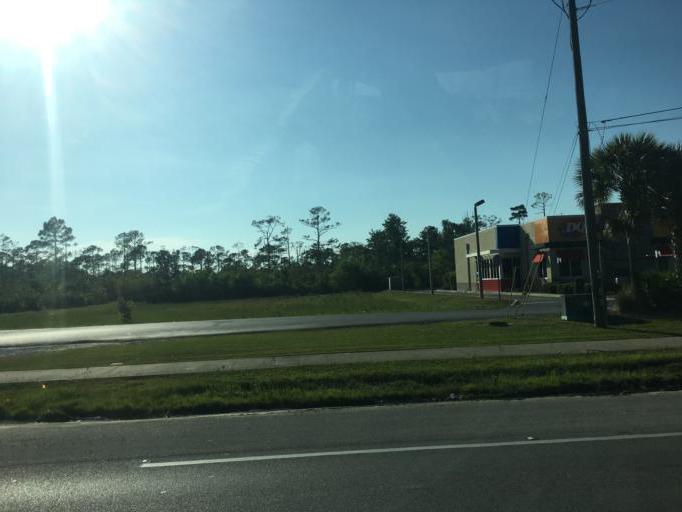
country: US
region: Florida
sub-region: Bay County
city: Panama City Beach
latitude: 30.1994
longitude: -85.8209
